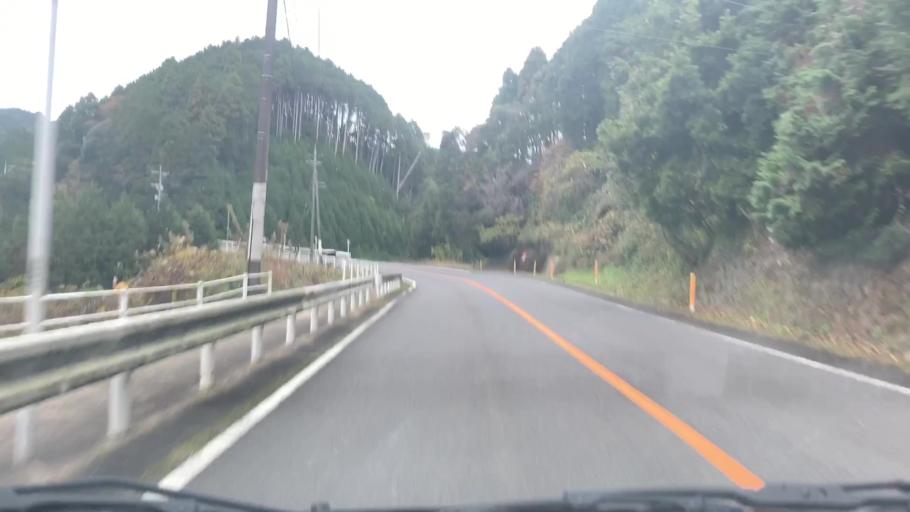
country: JP
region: Saga Prefecture
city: Ureshinomachi-shimojuku
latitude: 33.1582
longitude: 129.9712
